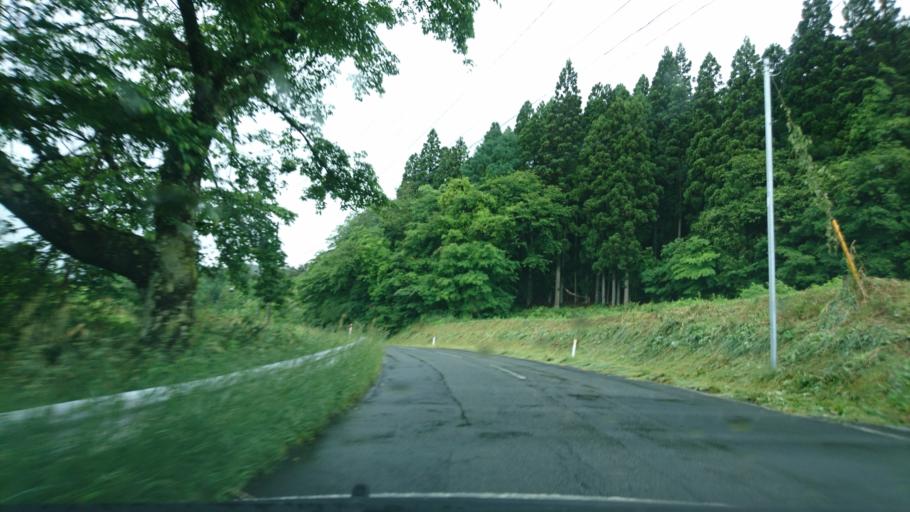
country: JP
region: Iwate
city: Ichinoseki
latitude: 38.9739
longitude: 140.9880
